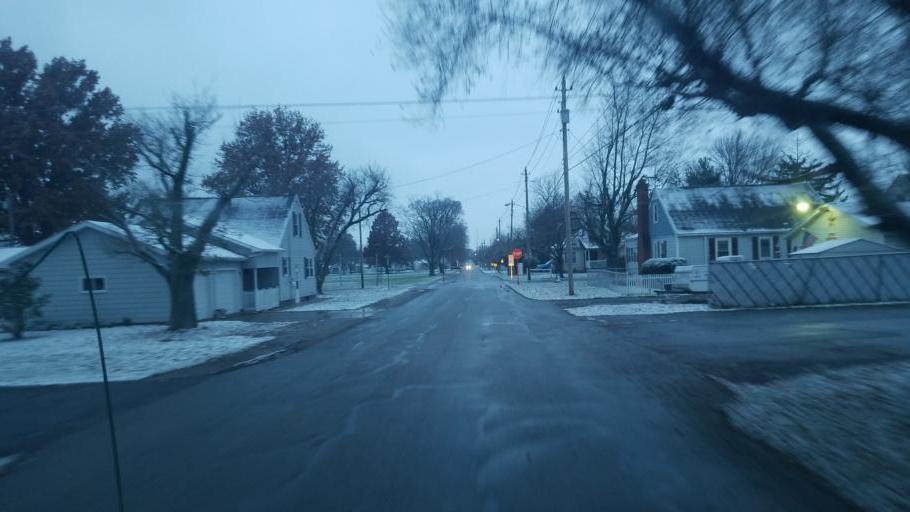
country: US
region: Ohio
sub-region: Marion County
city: Marion
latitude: 40.5855
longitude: -83.1016
